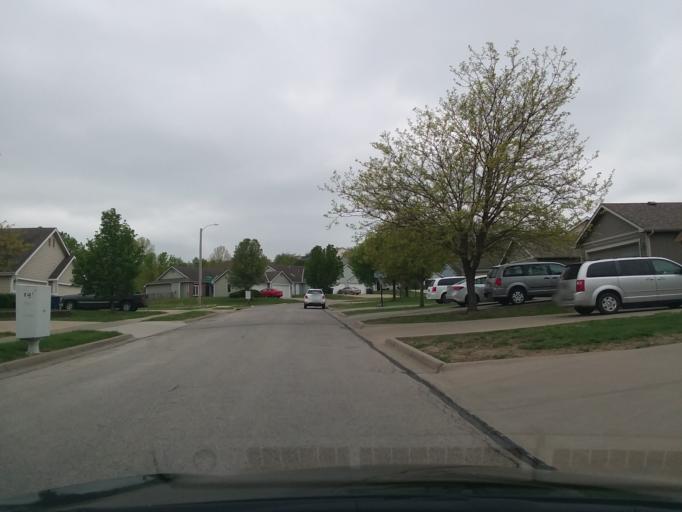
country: US
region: Kansas
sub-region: Douglas County
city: Lawrence
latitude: 38.9946
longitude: -95.2824
